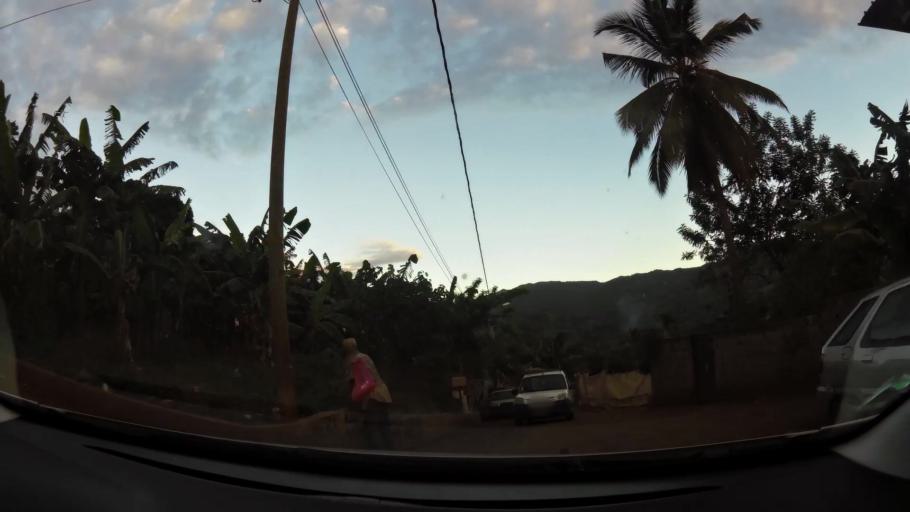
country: YT
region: Koungou
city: Koungou
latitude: -12.7330
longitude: 45.1643
